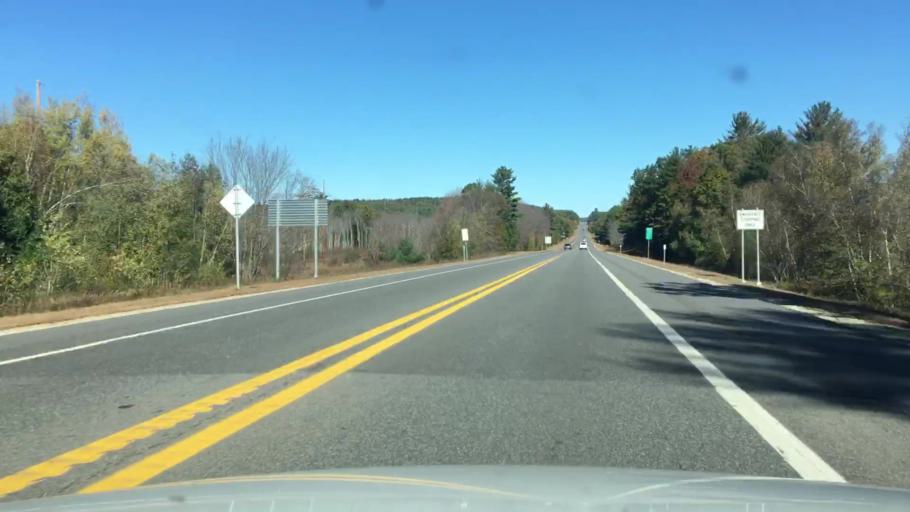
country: US
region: New Hampshire
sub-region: Strafford County
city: Rochester
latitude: 43.3402
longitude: -70.9842
